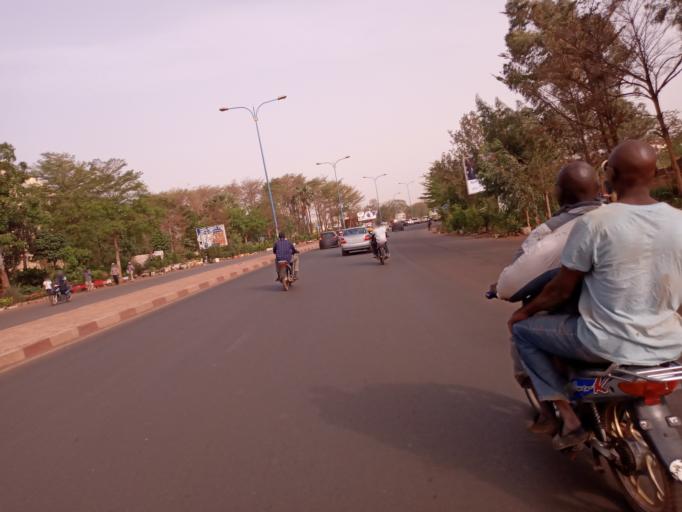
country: ML
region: Bamako
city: Bamako
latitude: 12.6392
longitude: -8.0197
